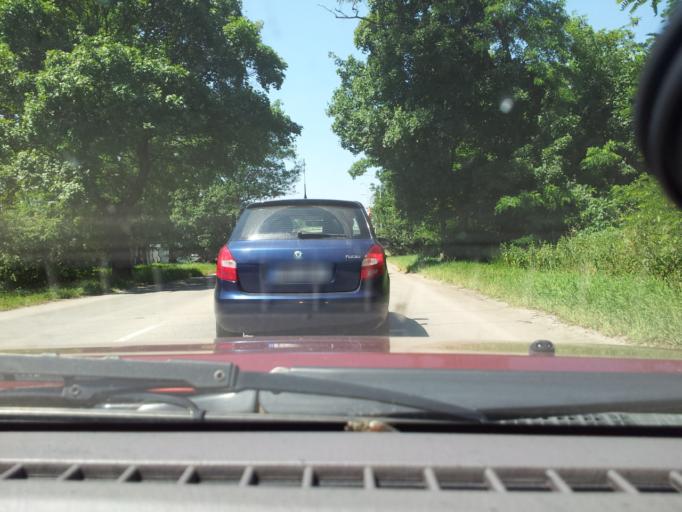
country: CZ
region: South Moravian
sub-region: Mesto Brno
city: Brno
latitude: 49.1593
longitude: 16.6414
